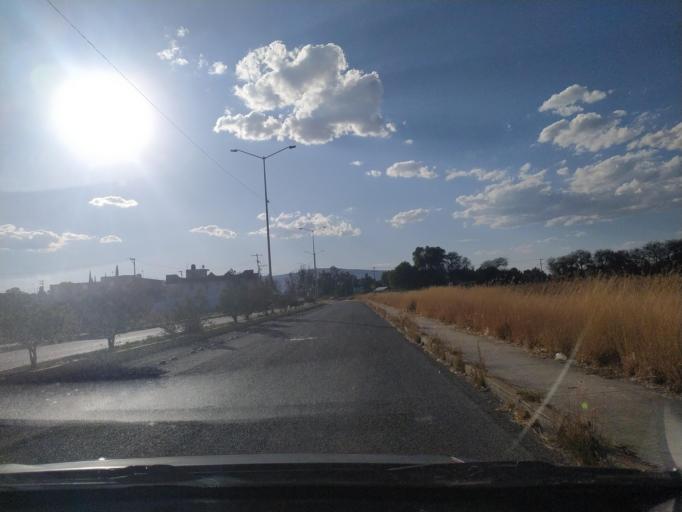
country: MX
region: Guanajuato
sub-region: San Francisco del Rincon
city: Fraccionamiento la Mezquitera
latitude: 21.0119
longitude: -101.8330
